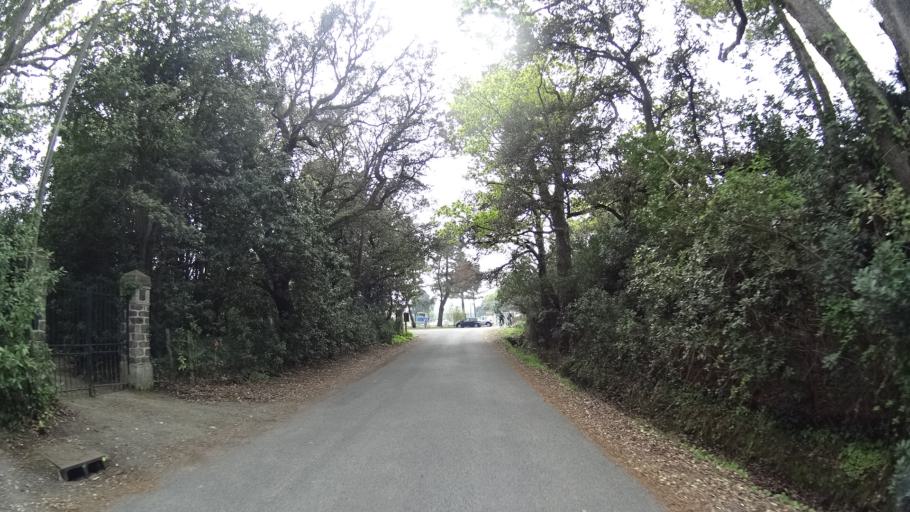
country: FR
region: Pays de la Loire
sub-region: Departement de la Vendee
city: La Gueriniere
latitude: 47.0108
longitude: -2.2307
